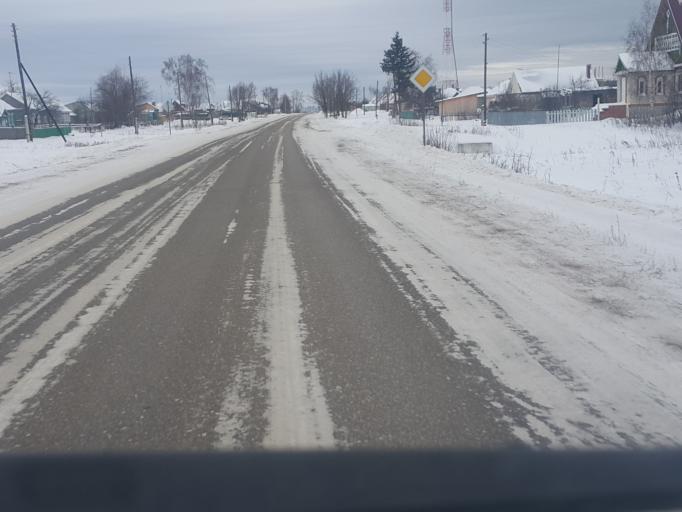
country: RU
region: Tambov
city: Platonovka
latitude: 52.8349
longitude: 41.8116
